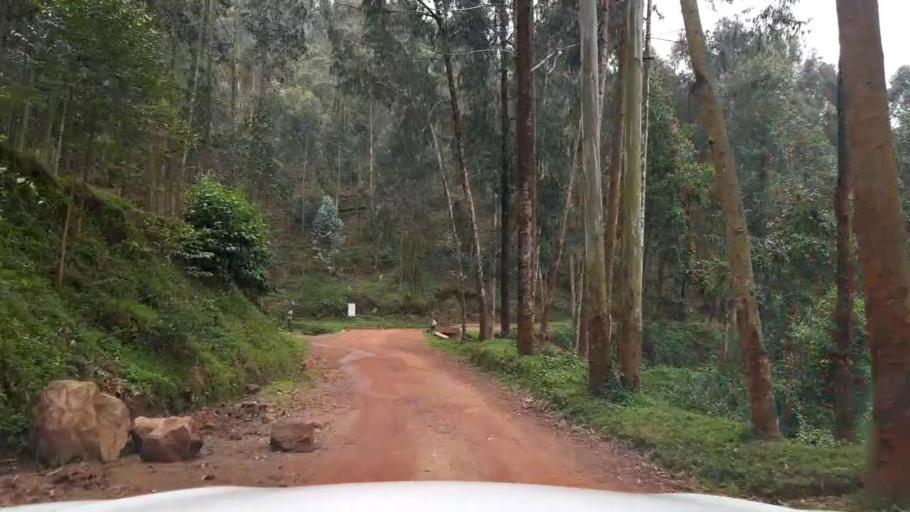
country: UG
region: Western Region
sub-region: Kabale District
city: Kabale
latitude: -1.4241
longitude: 29.8688
